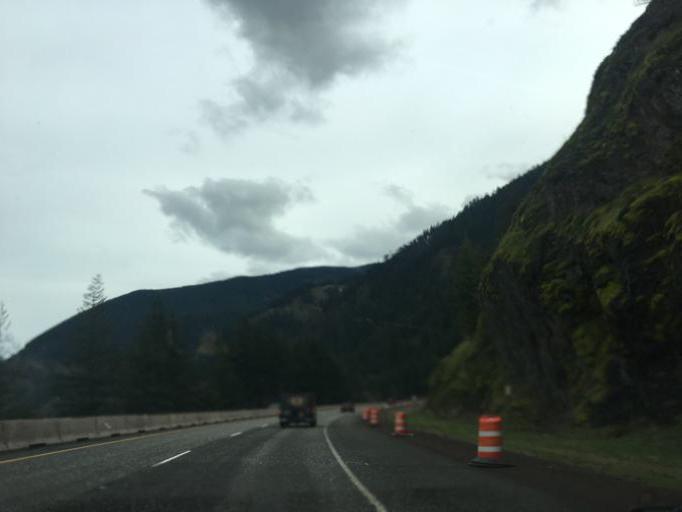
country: US
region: Washington
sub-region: Skamania County
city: Carson
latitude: 45.6902
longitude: -121.7190
